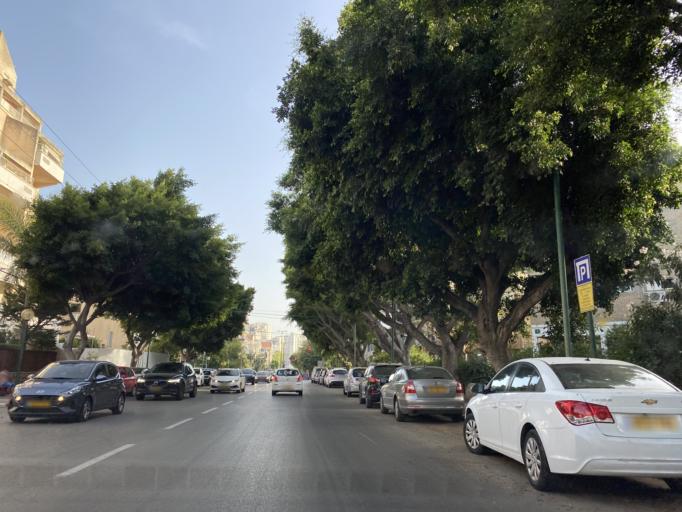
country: IL
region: Central District
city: Kfar Saba
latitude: 32.1758
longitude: 34.9025
